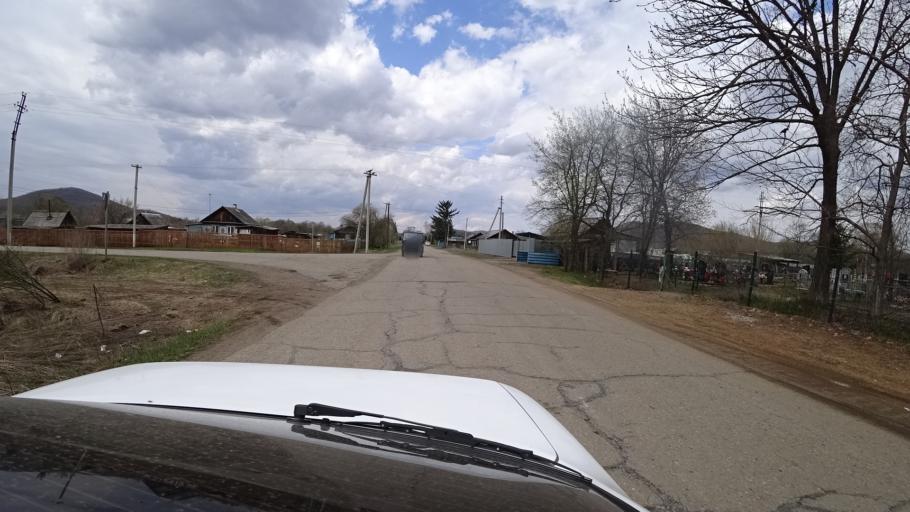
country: RU
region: Primorskiy
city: Novopokrovka
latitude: 45.6056
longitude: 134.2792
